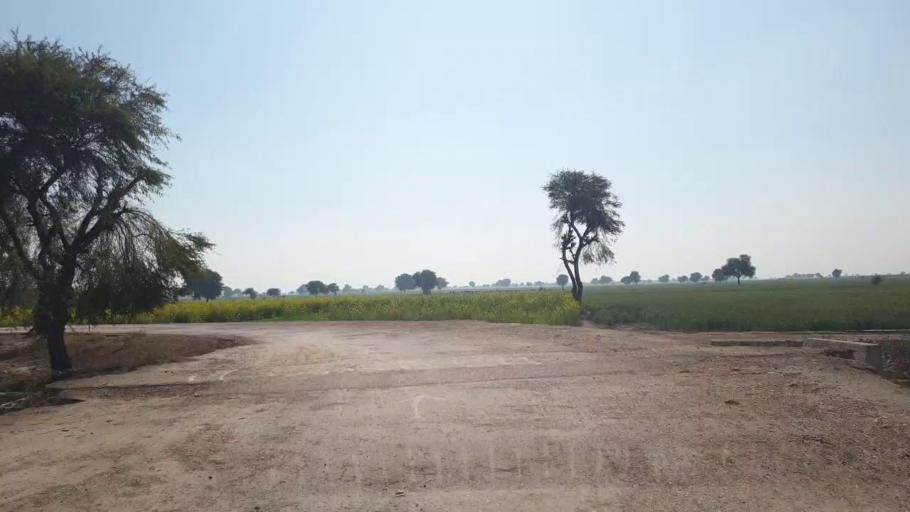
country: PK
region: Sindh
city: Shahpur Chakar
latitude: 26.1083
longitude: 68.6288
